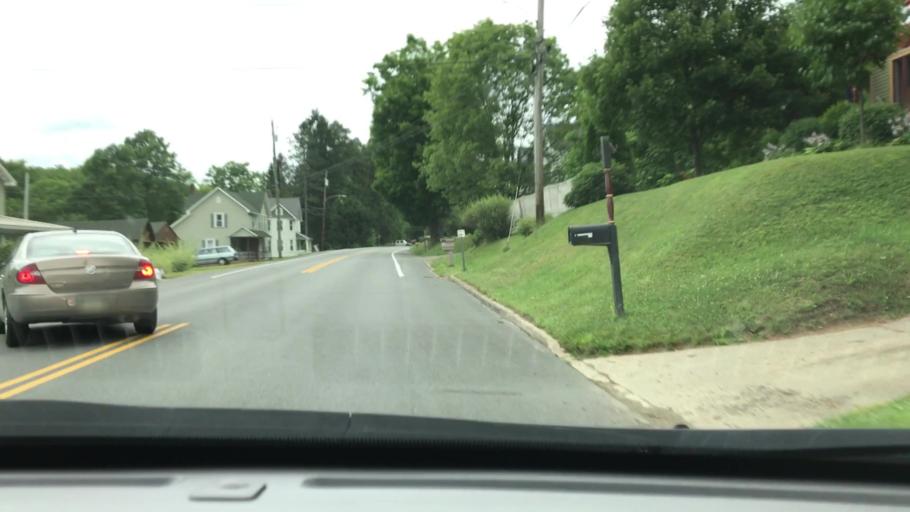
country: US
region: Pennsylvania
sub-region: Elk County
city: Johnsonburg
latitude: 41.5791
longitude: -78.6884
